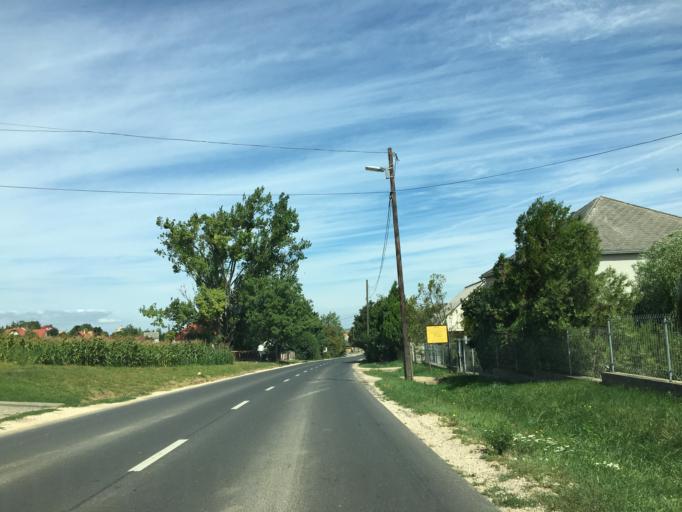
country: HU
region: Fejer
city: Many
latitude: 47.5893
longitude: 18.6652
